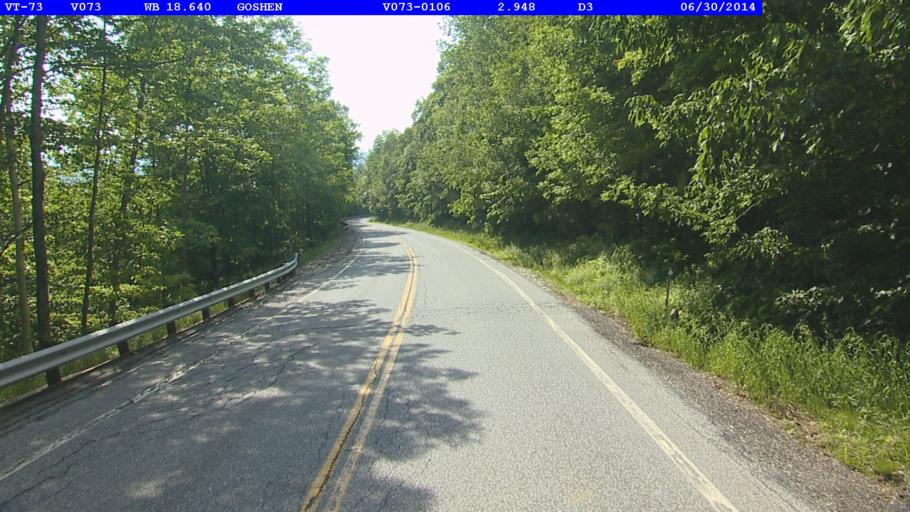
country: US
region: Vermont
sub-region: Rutland County
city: Brandon
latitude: 43.8430
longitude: -72.9752
